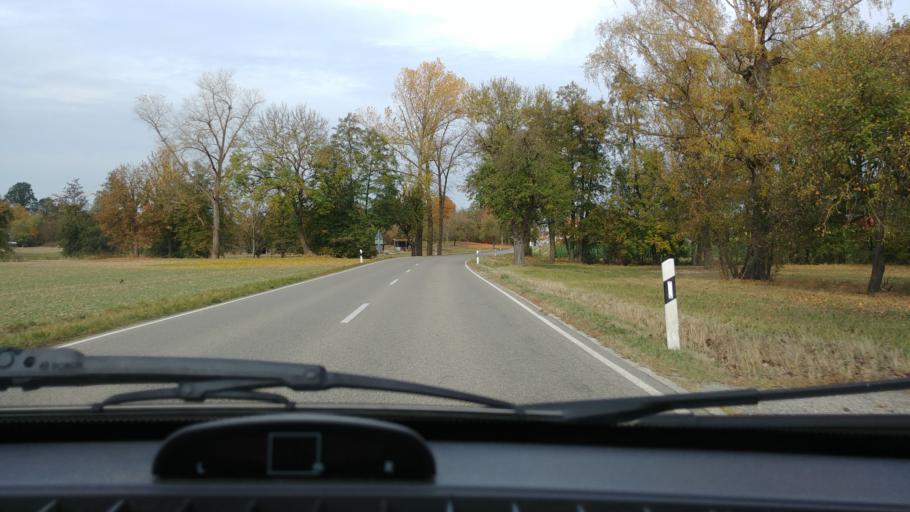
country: DE
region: Baden-Wuerttemberg
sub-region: Regierungsbezirk Stuttgart
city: Stimpfach
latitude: 49.0875
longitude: 10.0657
